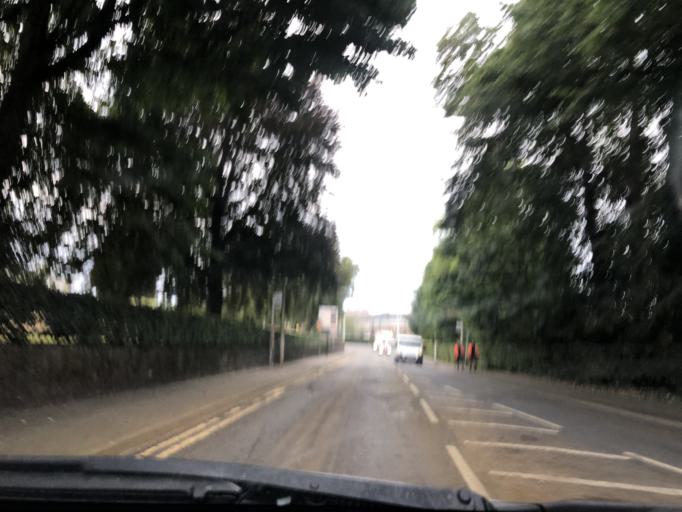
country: GB
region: England
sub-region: Kent
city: Sevenoaks
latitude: 51.2641
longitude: 0.1943
